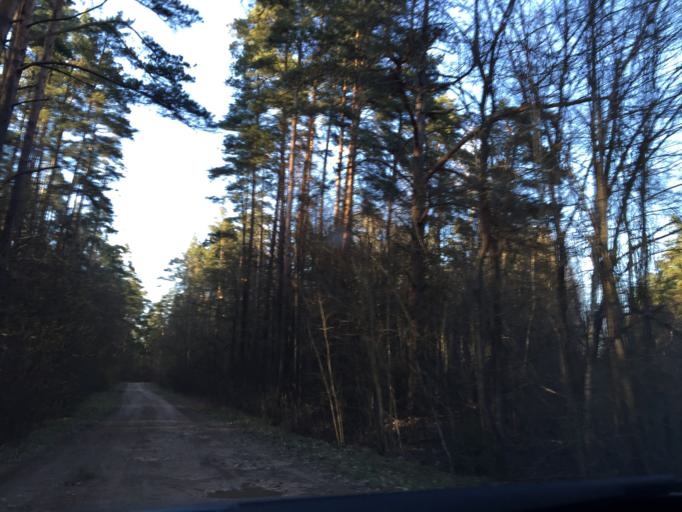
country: LV
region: Kekava
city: Kekava
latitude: 56.8553
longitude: 24.2321
